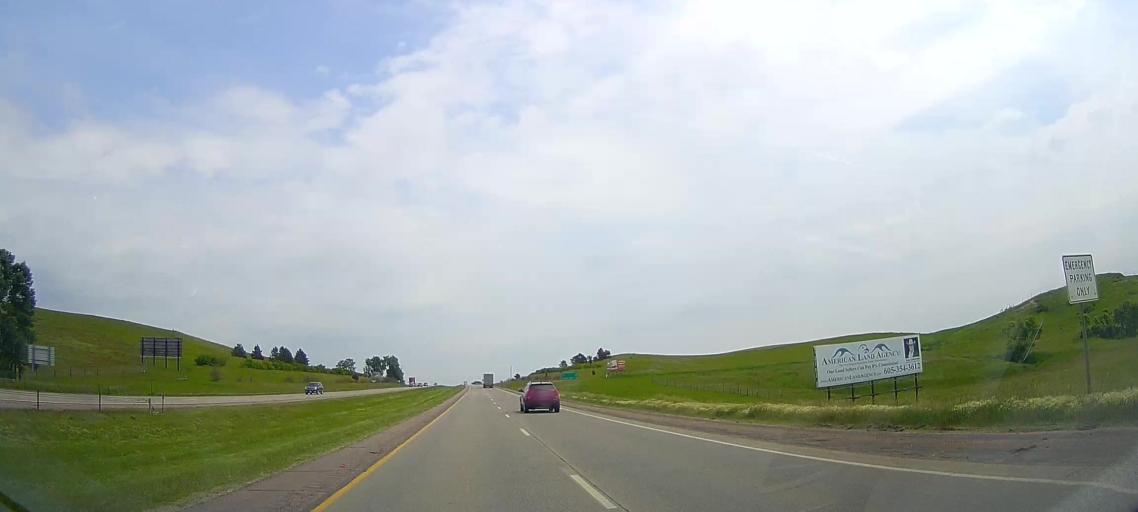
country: US
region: South Dakota
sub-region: Minnehaha County
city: Hartford
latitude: 43.6086
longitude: -96.8778
